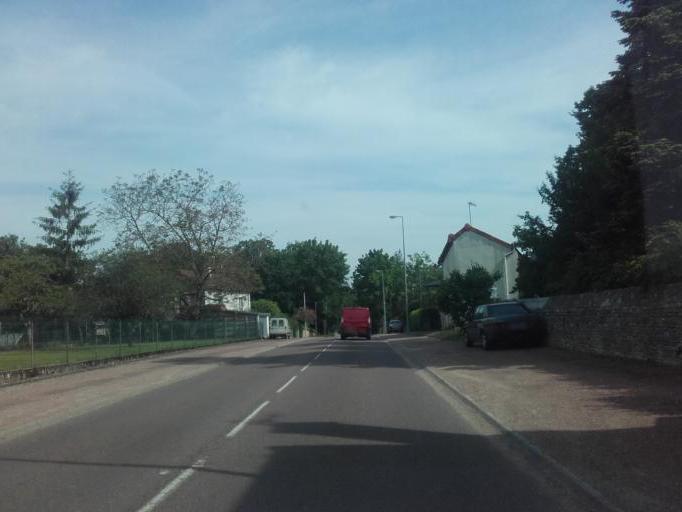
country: FR
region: Bourgogne
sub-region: Departement de Saone-et-Loire
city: Dracy-le-Fort
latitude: 46.8124
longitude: 4.7528
